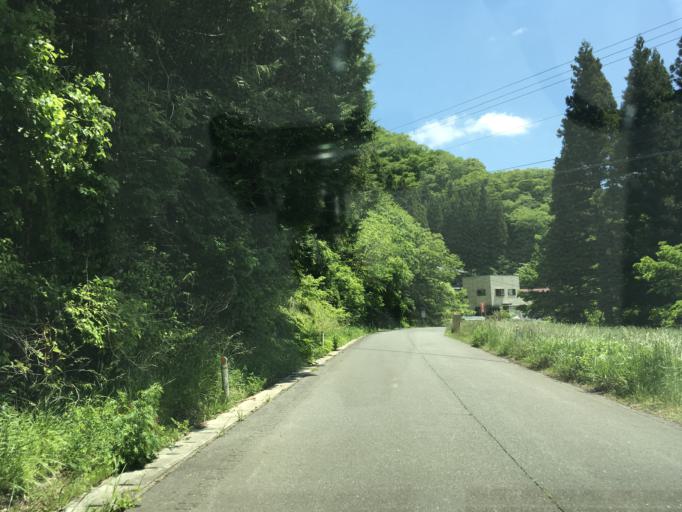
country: JP
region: Miyagi
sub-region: Oshika Gun
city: Onagawa Cho
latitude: 38.6748
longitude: 141.3522
